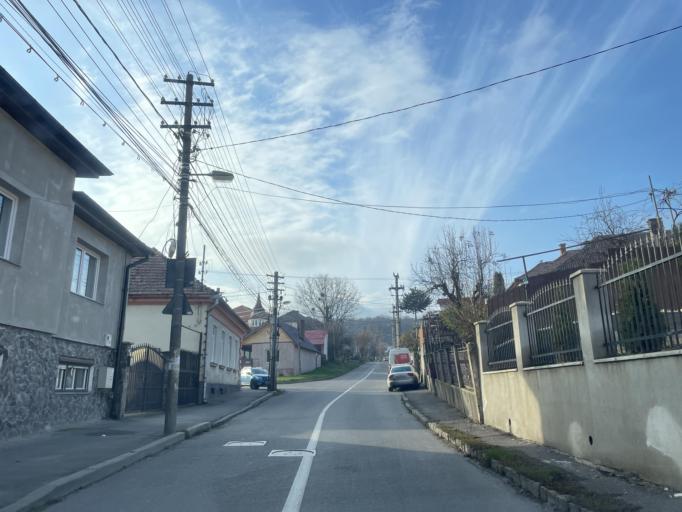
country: RO
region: Mures
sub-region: Municipiul Reghin
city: Reghin
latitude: 46.7845
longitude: 24.6983
